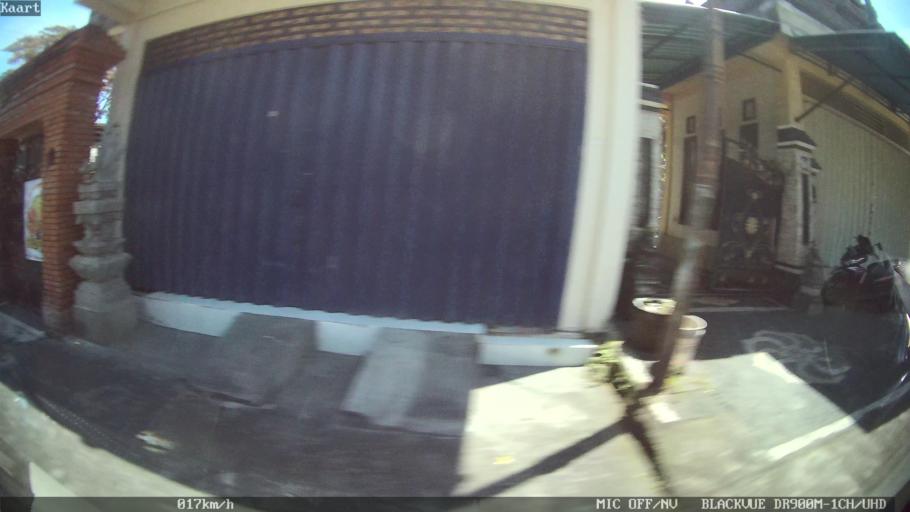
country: ID
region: Bali
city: Banjar Kelodan
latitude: -8.5529
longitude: 115.3354
